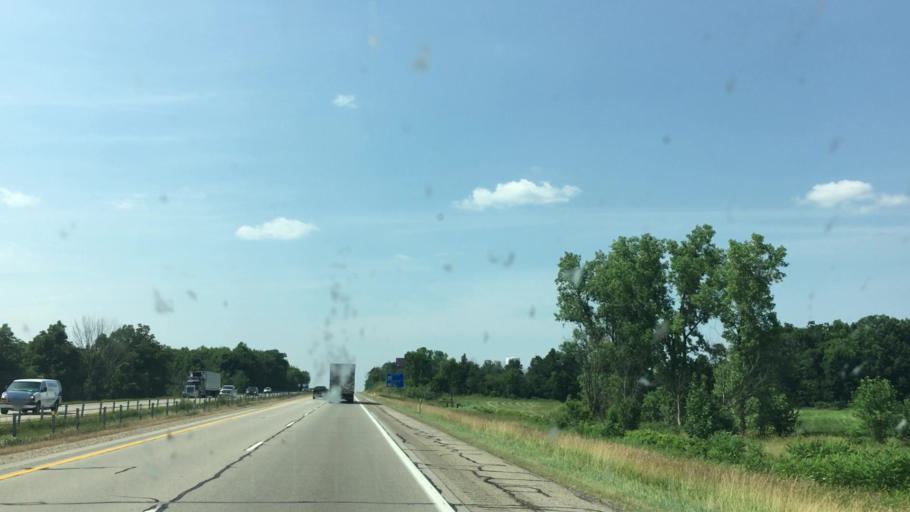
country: US
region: Michigan
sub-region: Allegan County
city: Wayland
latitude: 42.7149
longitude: -85.6649
